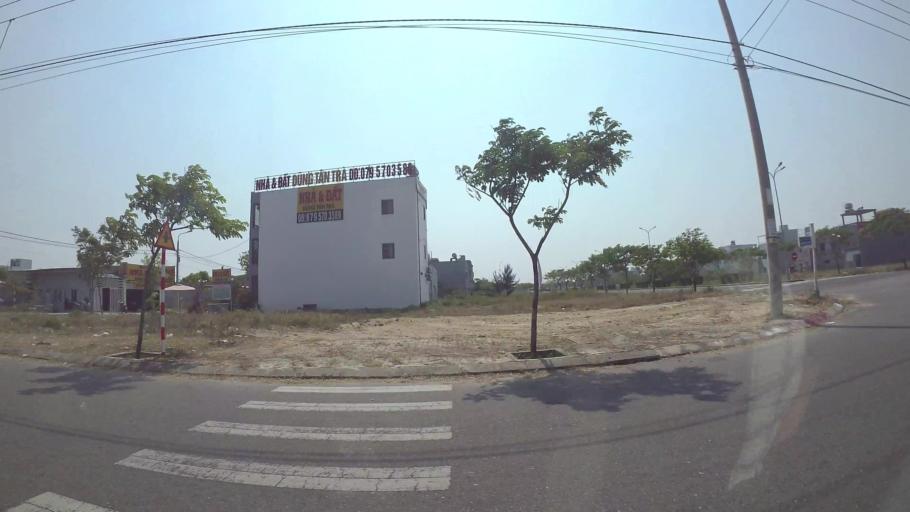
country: VN
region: Da Nang
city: Ngu Hanh Son
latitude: 15.9856
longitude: 108.2705
